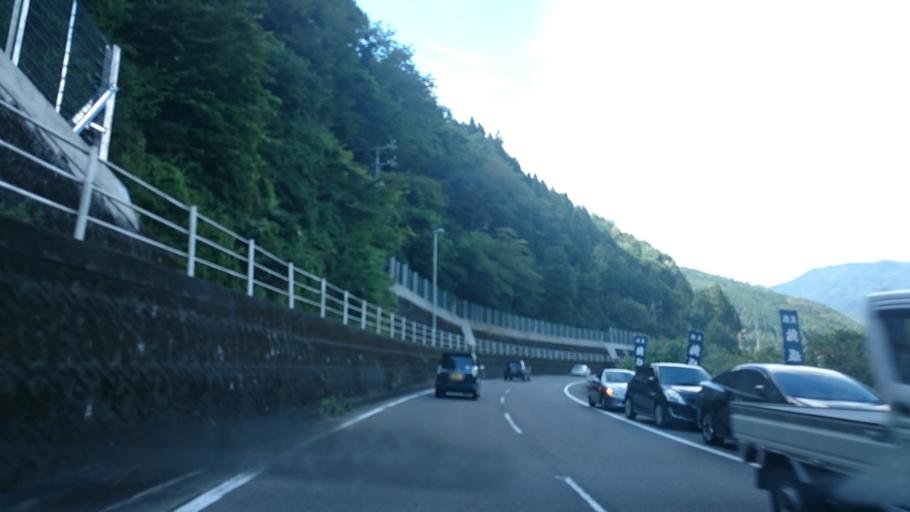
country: JP
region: Gifu
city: Nakatsugawa
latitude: 35.6087
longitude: 137.4600
